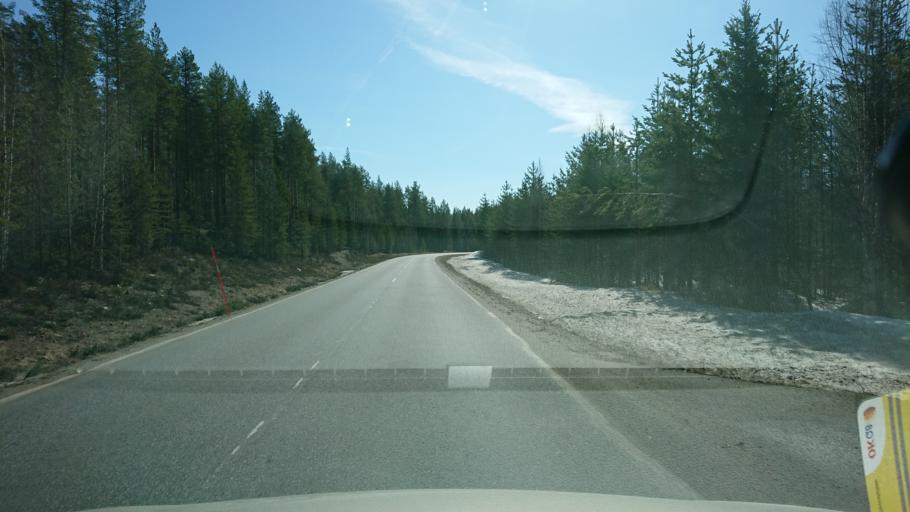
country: SE
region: Vaesterbotten
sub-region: Dorotea Kommun
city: Dorotea
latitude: 64.0139
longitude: 16.2908
